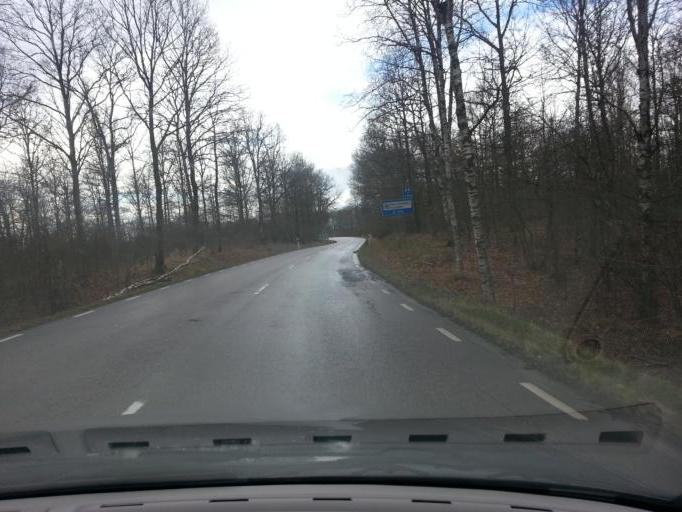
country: SE
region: Skane
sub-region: Klippans Kommun
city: Ljungbyhed
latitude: 56.0795
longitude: 13.2560
